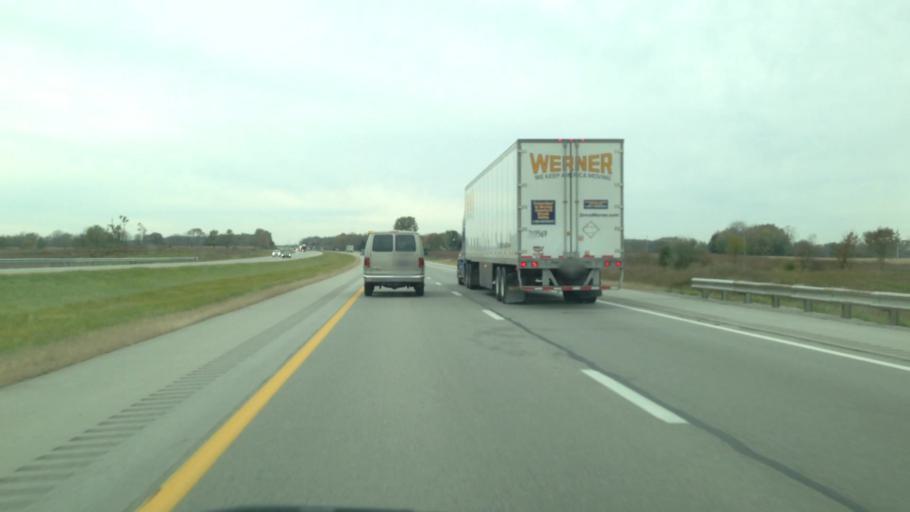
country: US
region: Ohio
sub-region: Williams County
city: Montpelier
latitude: 41.6268
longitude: -84.7107
